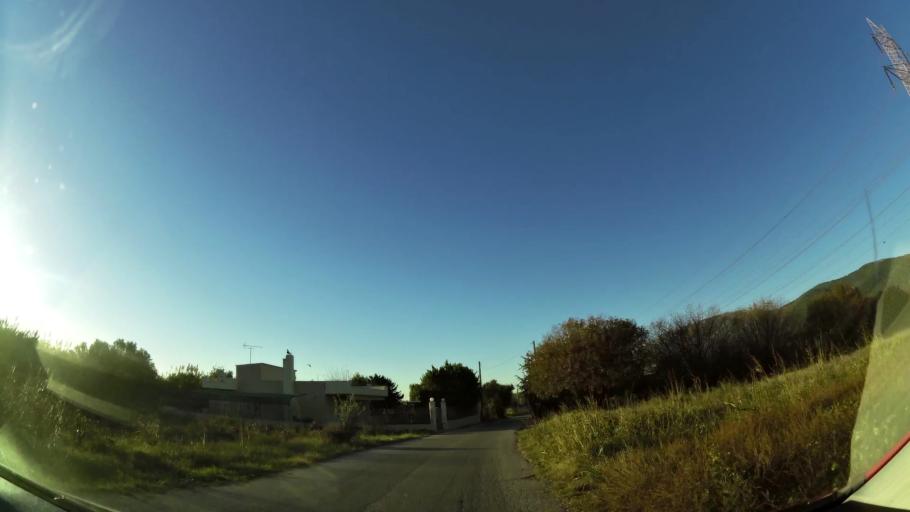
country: GR
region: Attica
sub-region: Nomarchia Anatolikis Attikis
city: Pallini
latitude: 38.0026
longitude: 23.8645
